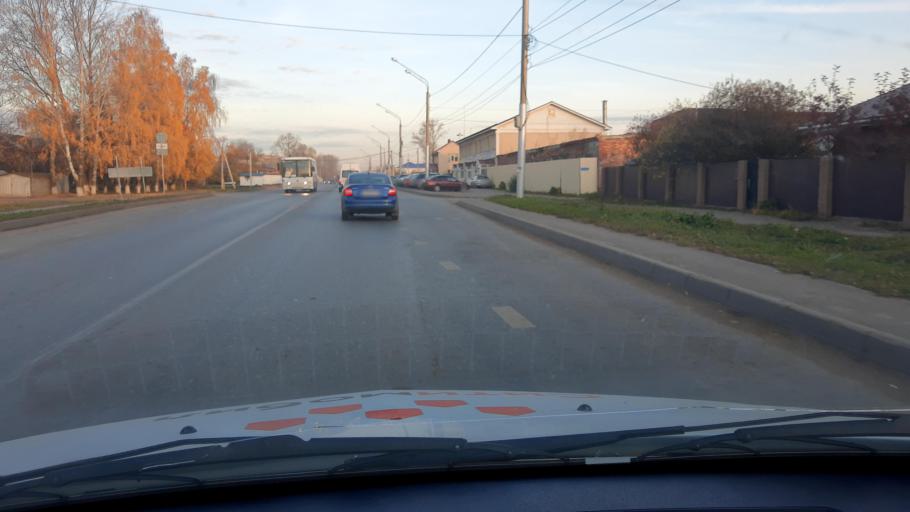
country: RU
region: Bashkortostan
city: Iglino
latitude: 54.7631
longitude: 56.2366
